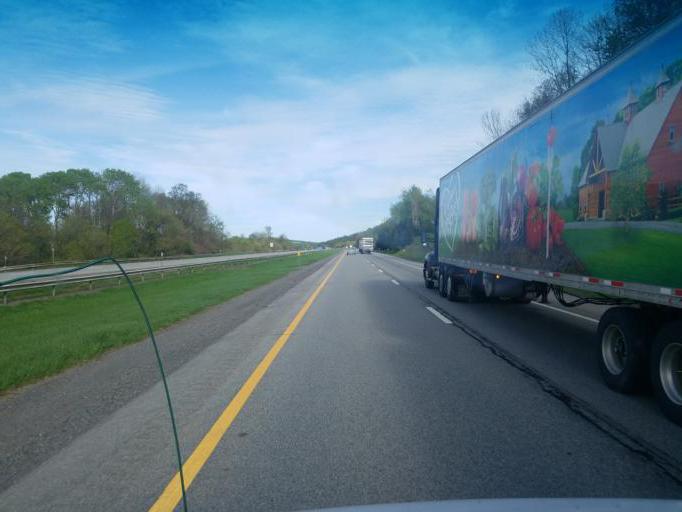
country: US
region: New York
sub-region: Herkimer County
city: Little Falls
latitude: 43.0102
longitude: -74.9136
